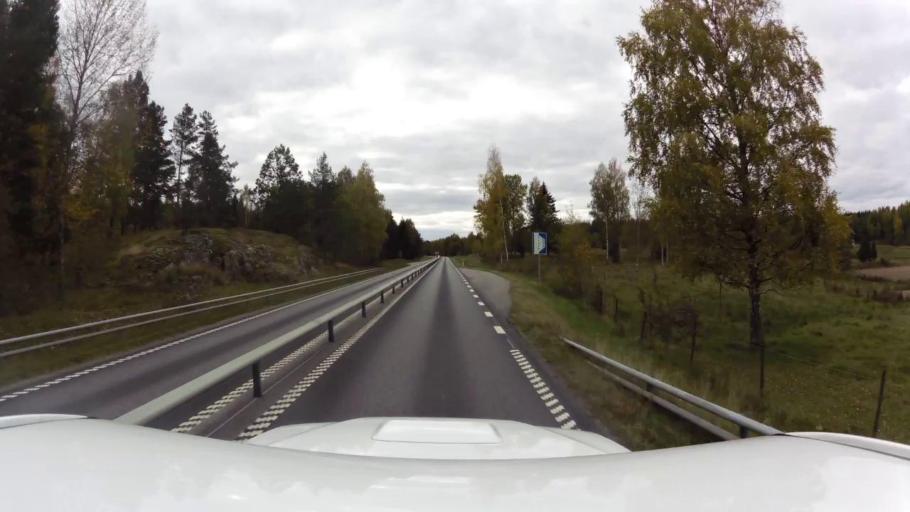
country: SE
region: OEstergoetland
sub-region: Linkopings Kommun
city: Malmslatt
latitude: 58.2970
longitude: 15.5641
